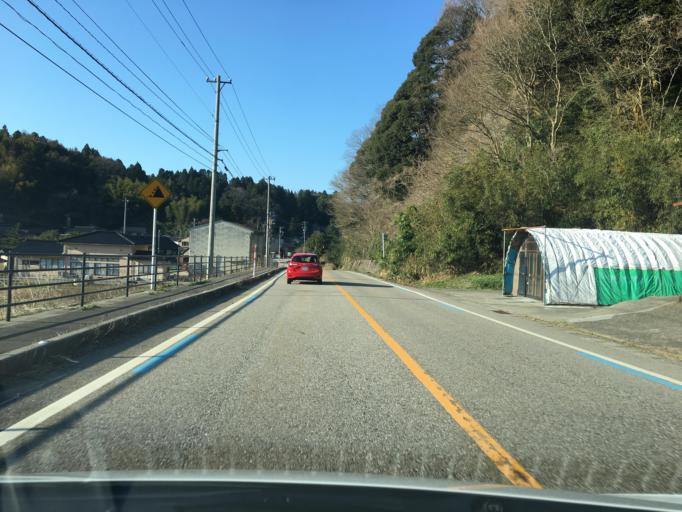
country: JP
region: Toyama
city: Himi
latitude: 36.9301
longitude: 137.0262
